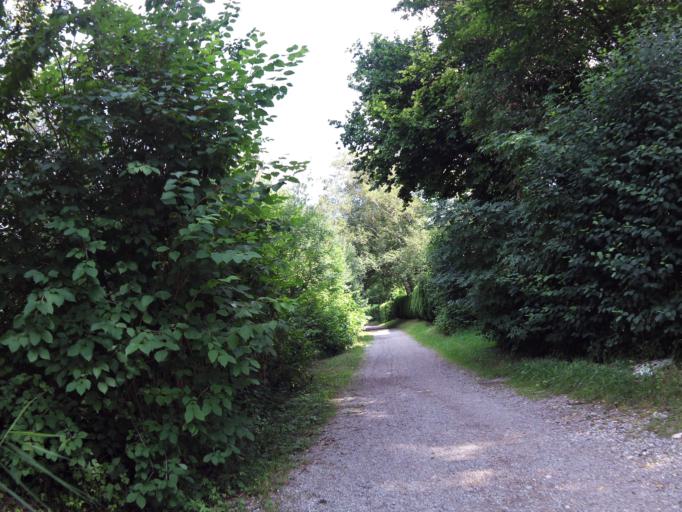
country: DE
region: Bavaria
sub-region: Upper Bavaria
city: Andechs
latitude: 47.9705
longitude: 11.1496
